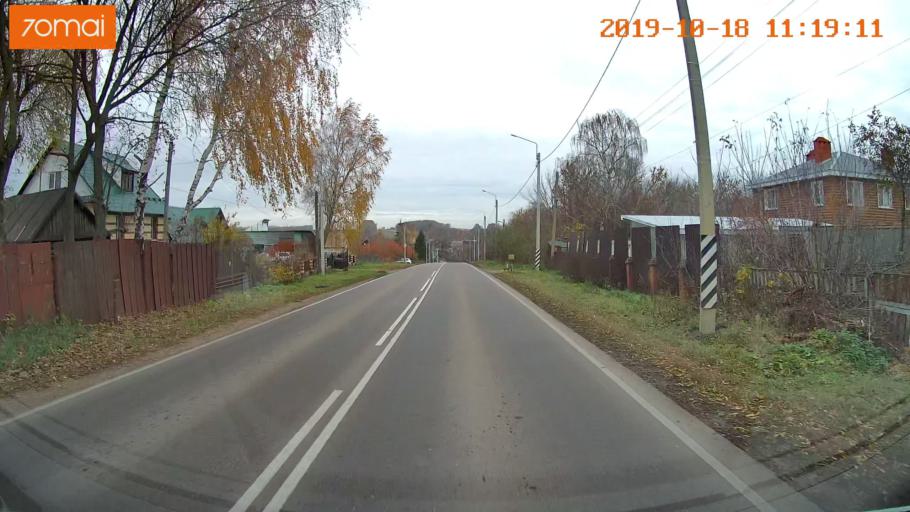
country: RU
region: Tula
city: Kimovsk
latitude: 54.0441
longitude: 38.5525
